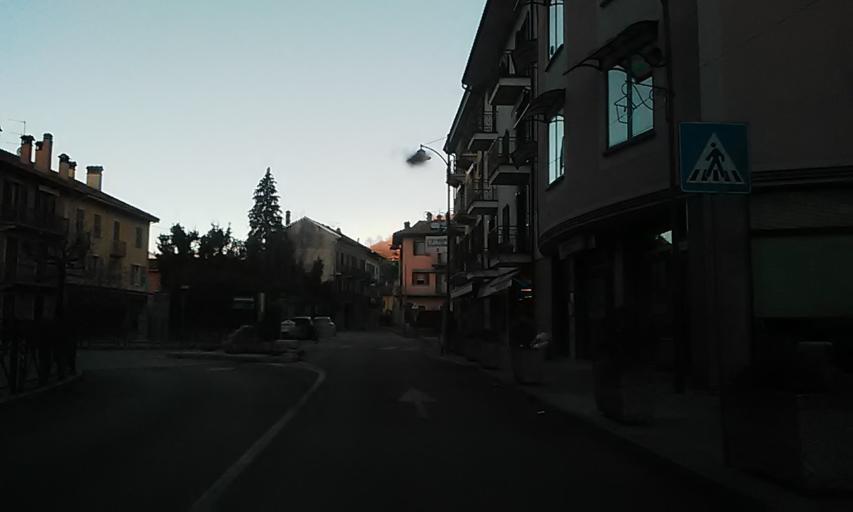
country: IT
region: Piedmont
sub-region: Provincia di Vercelli
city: Quarona
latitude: 45.7631
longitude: 8.2688
